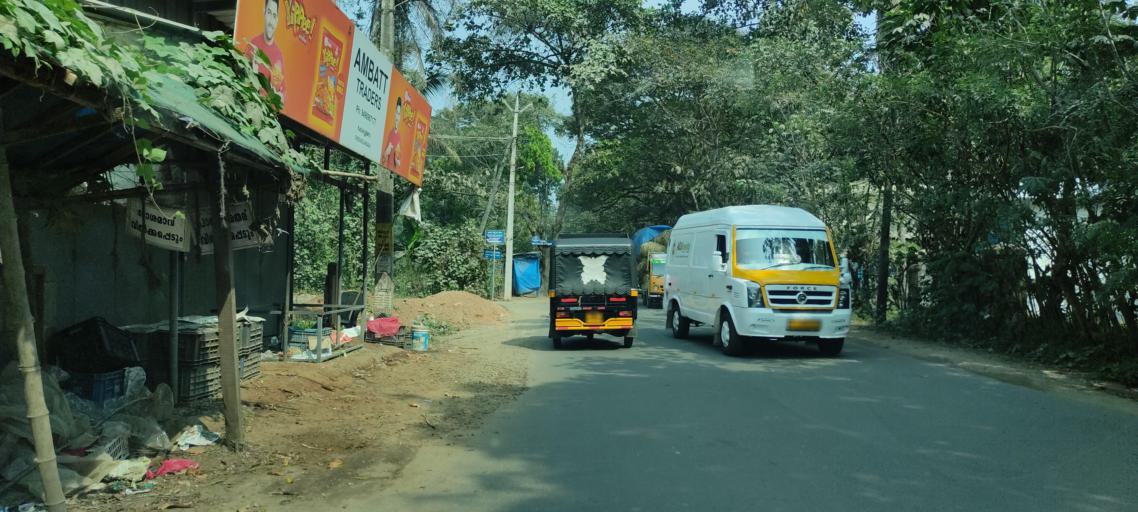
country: IN
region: Kerala
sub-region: Alappuzha
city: Shertallai
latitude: 9.6714
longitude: 76.4138
